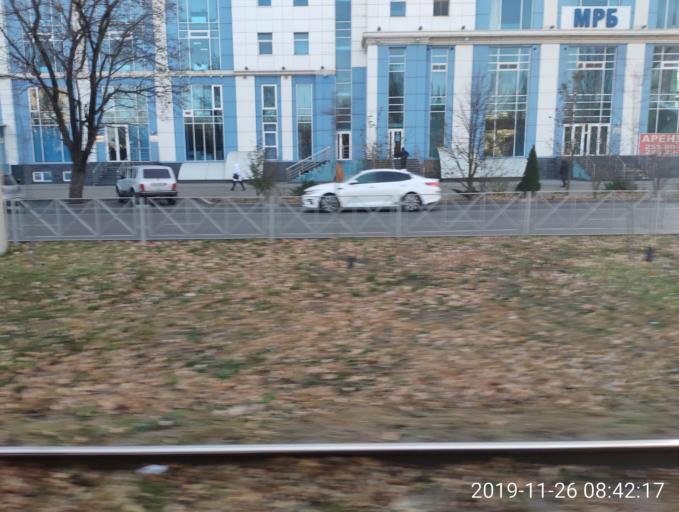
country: RU
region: Krasnodarskiy
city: Krasnodar
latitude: 45.0516
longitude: 38.9845
